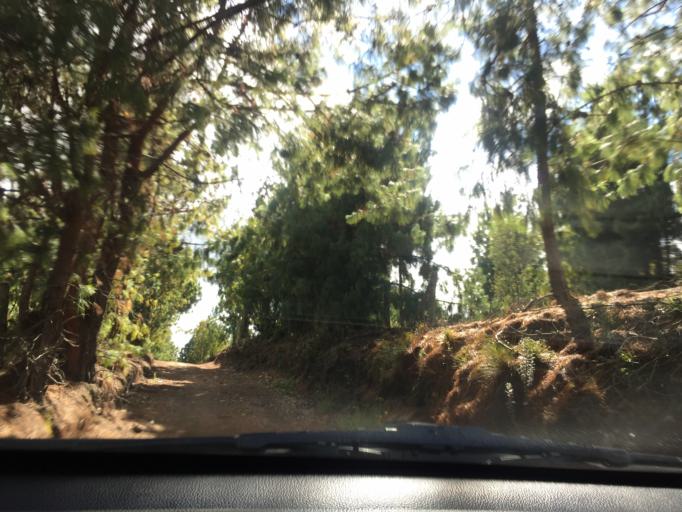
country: CO
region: Cundinamarca
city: Tocancipa
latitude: 4.9534
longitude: -73.8849
